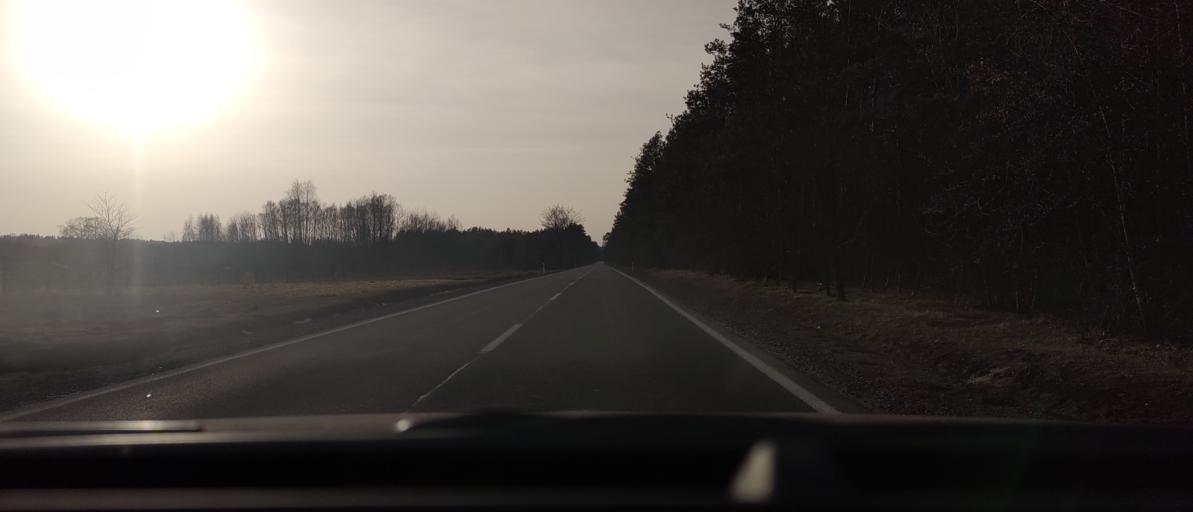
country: PL
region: Masovian Voivodeship
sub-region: Powiat bialobrzeski
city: Wysmierzyce
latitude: 51.6284
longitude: 20.8764
